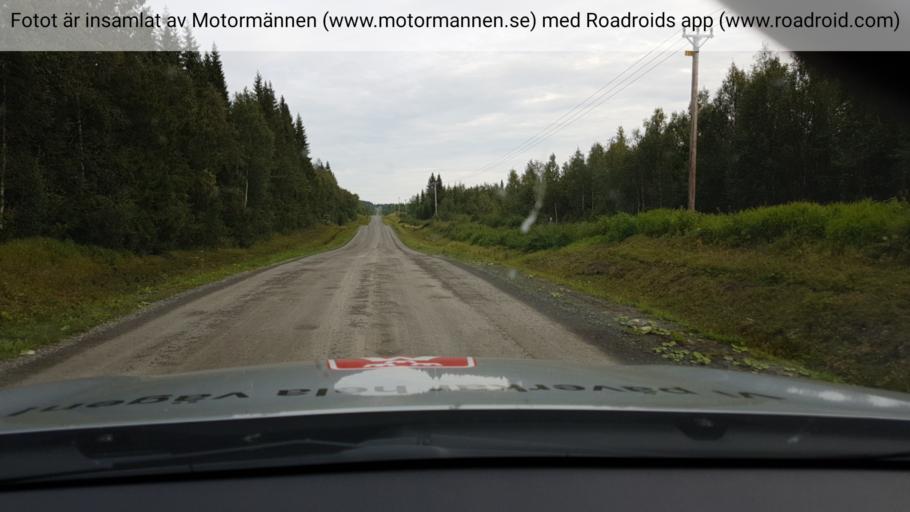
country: SE
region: Jaemtland
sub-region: OEstersunds Kommun
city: Lit
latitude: 63.6324
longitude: 14.9668
